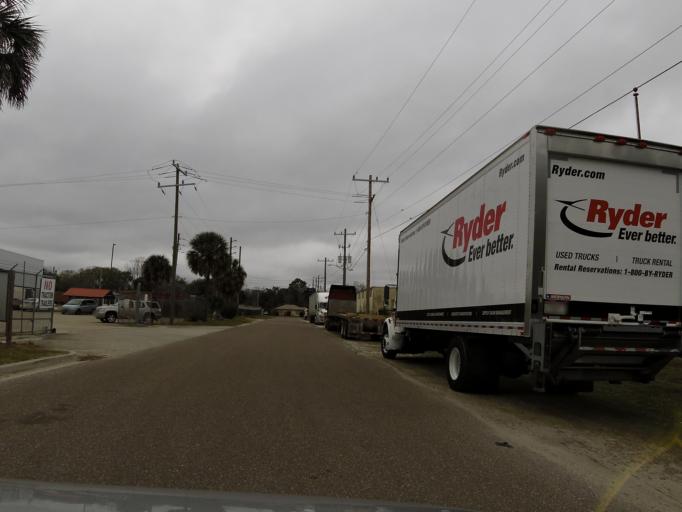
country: US
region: Florida
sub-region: Duval County
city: Jacksonville
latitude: 30.3670
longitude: -81.7130
